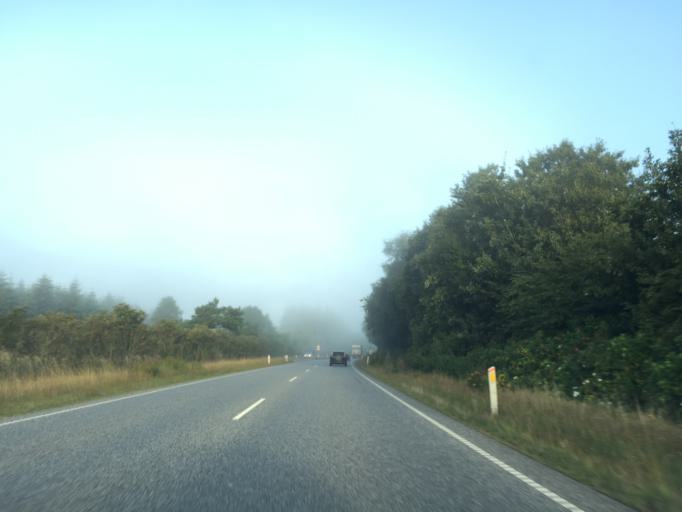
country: DK
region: Central Jutland
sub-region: Viborg Kommune
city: Bjerringbro
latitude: 56.3036
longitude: 9.6159
